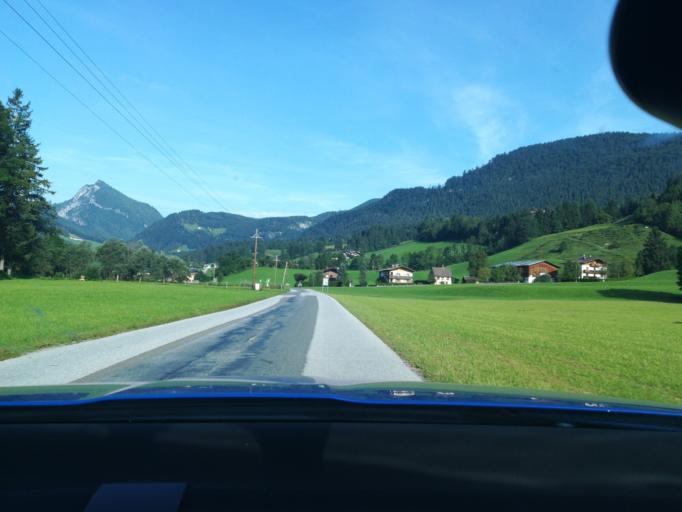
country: AT
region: Salzburg
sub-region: Politischer Bezirk Hallein
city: Abtenau
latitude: 47.5933
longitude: 13.3282
